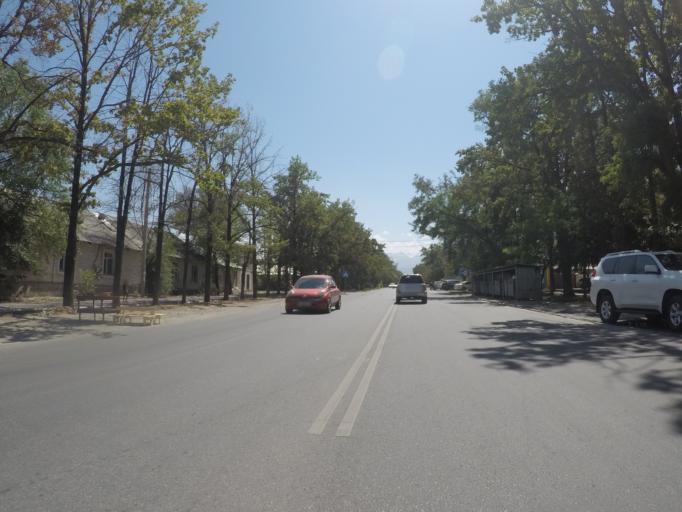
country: KG
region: Chuy
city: Bishkek
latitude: 42.8473
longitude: 74.5769
